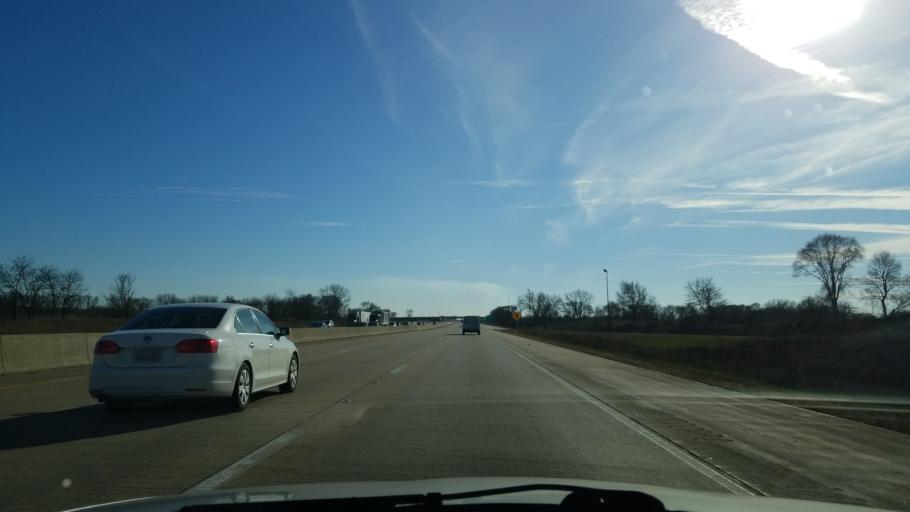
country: US
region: Illinois
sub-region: Winnebago County
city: South Beloit
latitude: 42.4799
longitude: -88.9952
